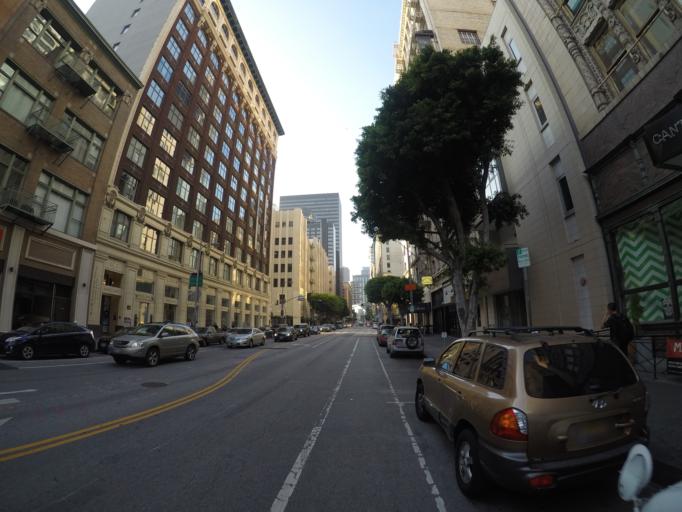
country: US
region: California
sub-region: Los Angeles County
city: Los Angeles
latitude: 34.0470
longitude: -118.2560
